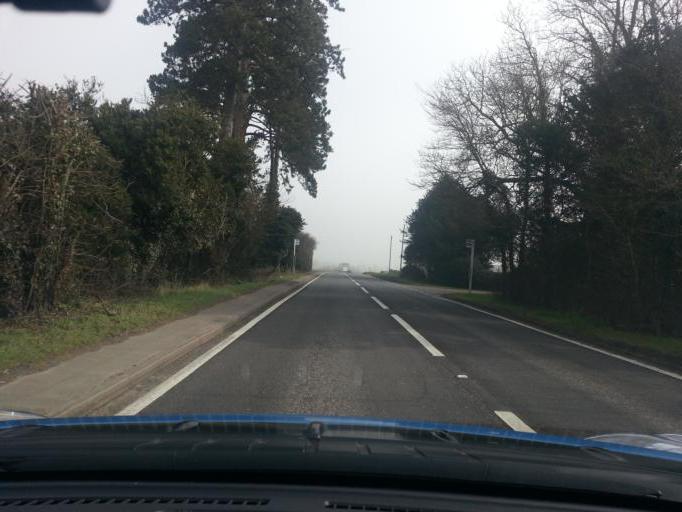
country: GB
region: England
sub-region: Oxfordshire
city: Faringdon
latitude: 51.6657
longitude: -1.5570
